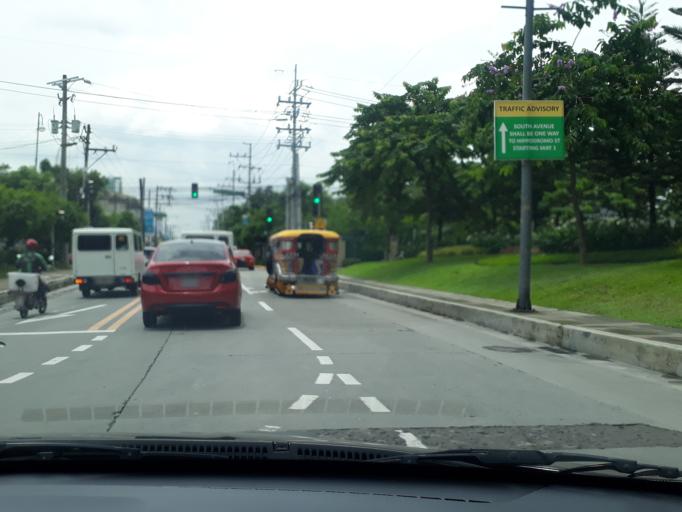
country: PH
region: Metro Manila
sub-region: Makati City
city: Makati City
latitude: 14.5638
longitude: 121.0161
